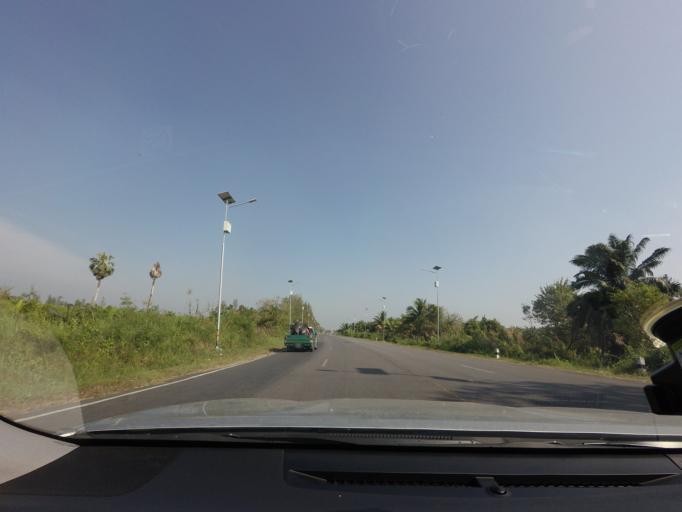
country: TH
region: Nakhon Si Thammarat
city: Nakhon Si Thammarat
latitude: 8.4694
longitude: 99.9810
